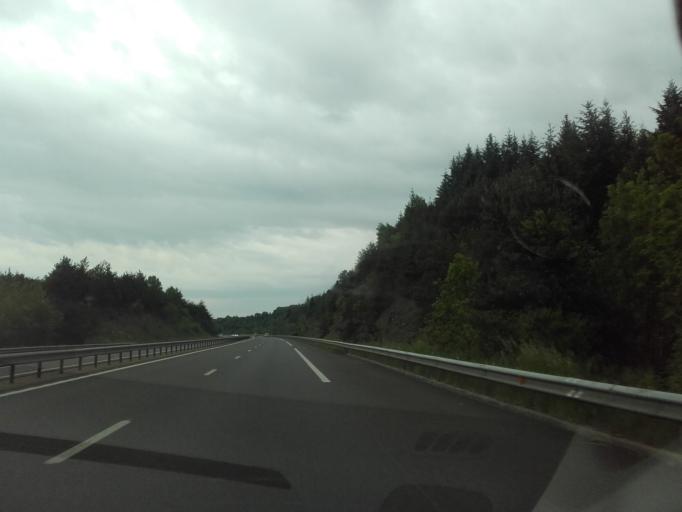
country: FR
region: Rhone-Alpes
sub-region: Departement de la Loire
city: Saint-Germain-Laval
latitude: 45.8633
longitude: 3.9645
